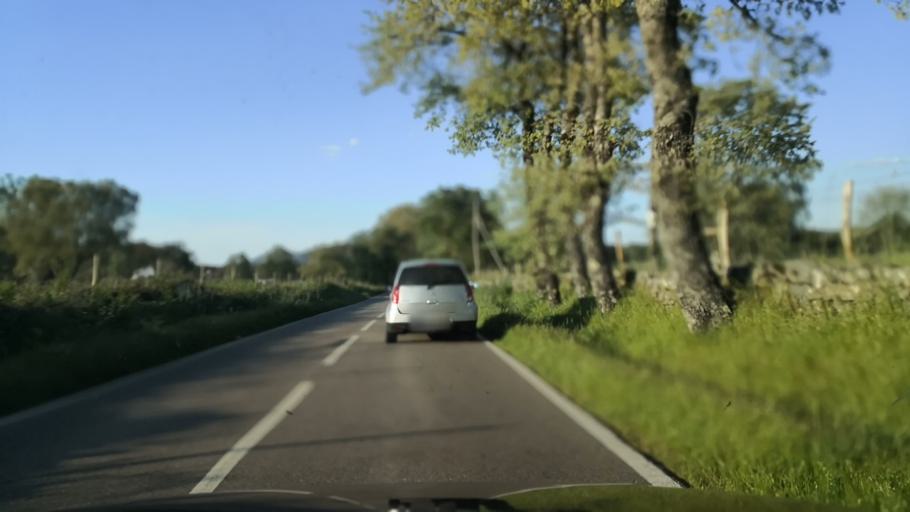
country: PT
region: Portalegre
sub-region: Portalegre
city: Reguengo
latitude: 39.3438
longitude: -7.4094
